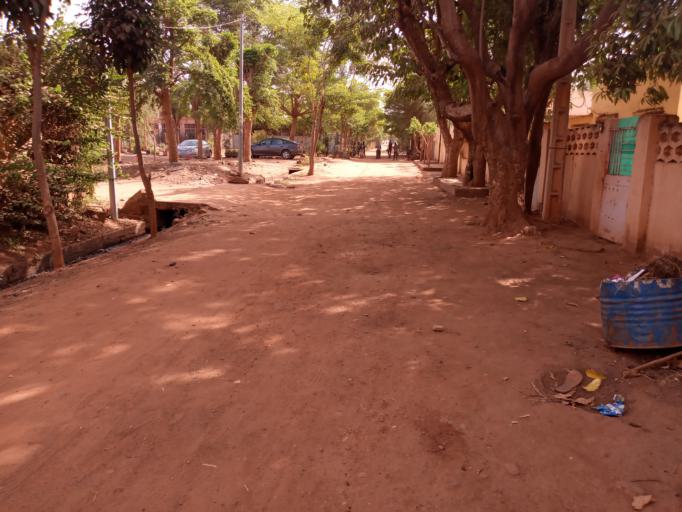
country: ML
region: Bamako
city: Bamako
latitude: 12.5875
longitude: -7.9497
